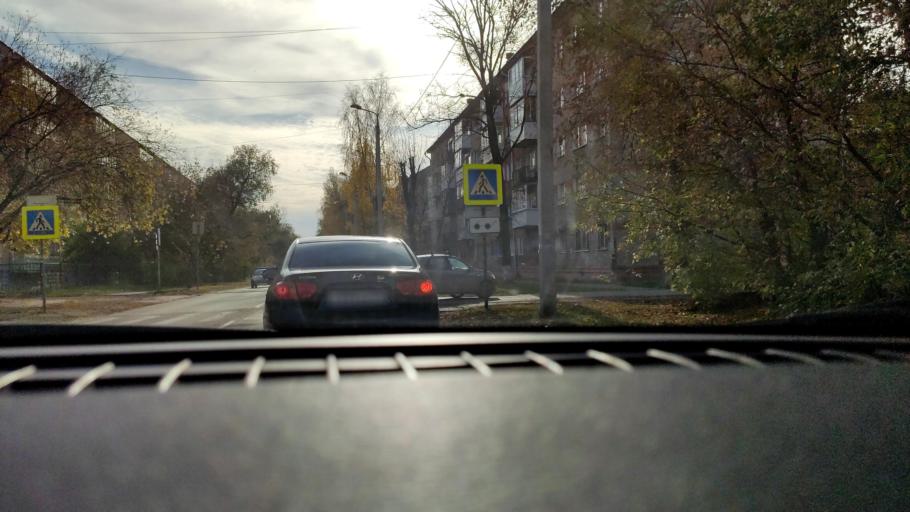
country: RU
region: Perm
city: Overyata
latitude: 58.0189
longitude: 55.9766
